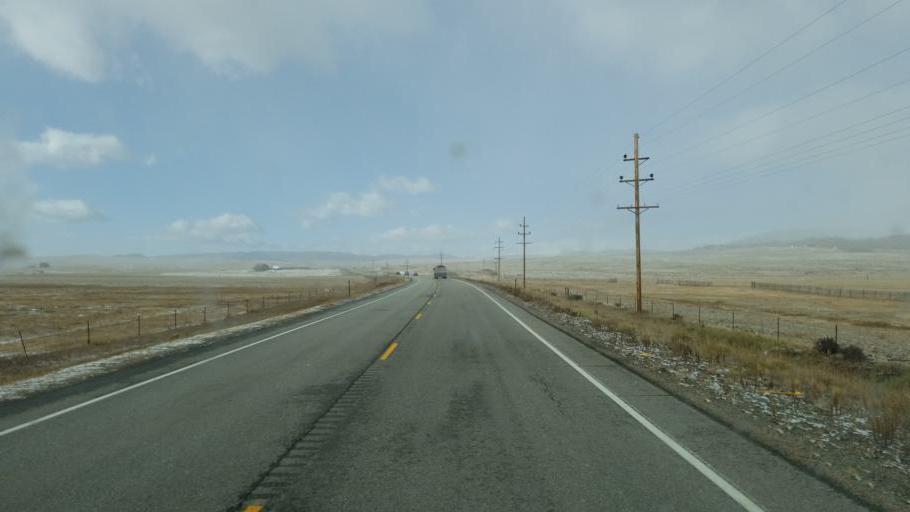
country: US
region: Colorado
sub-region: Park County
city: Fairplay
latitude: 39.3703
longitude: -105.8084
